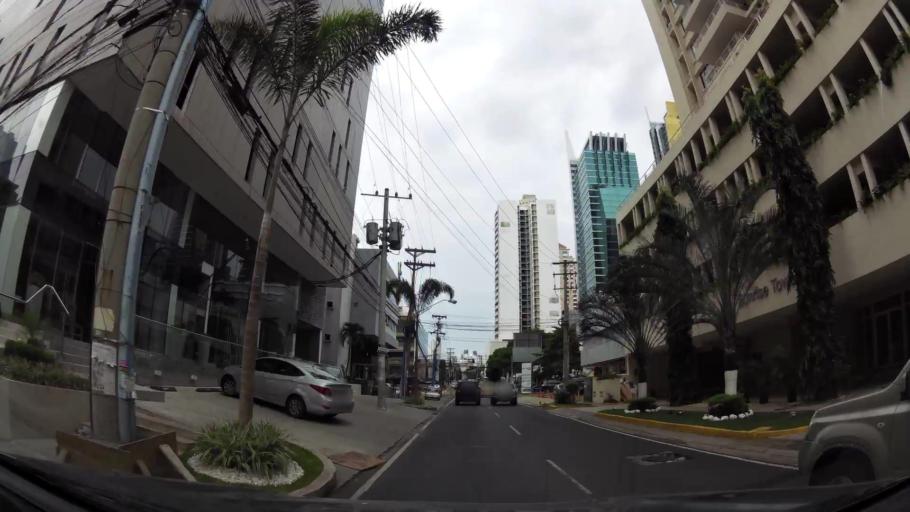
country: PA
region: Panama
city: Panama
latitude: 8.9829
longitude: -79.5211
